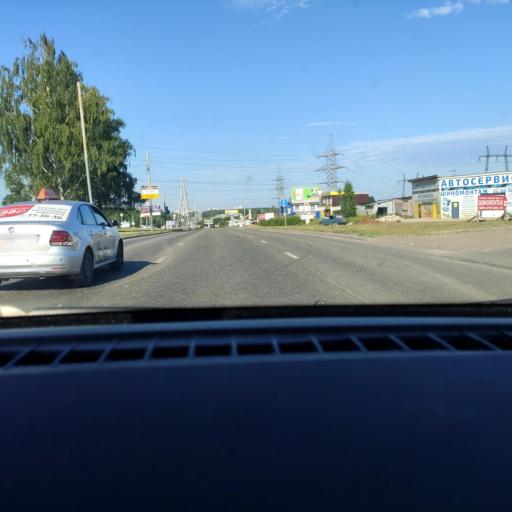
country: RU
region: Udmurtiya
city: Khokhryaki
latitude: 56.9002
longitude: 53.3133
